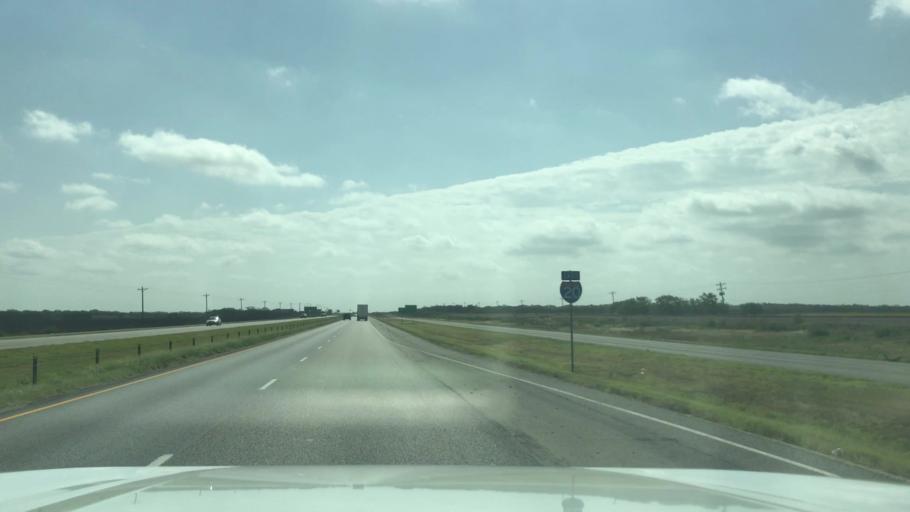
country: US
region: Texas
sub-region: Taylor County
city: Merkel
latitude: 32.4660
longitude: -99.9769
